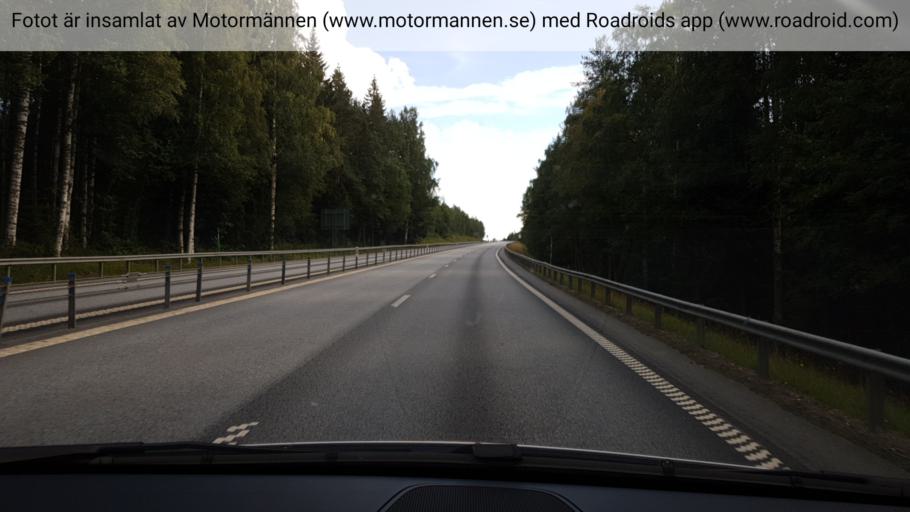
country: SE
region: Vaesterbotten
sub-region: Vannas Kommun
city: Vannasby
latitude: 63.9103
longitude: 19.8875
